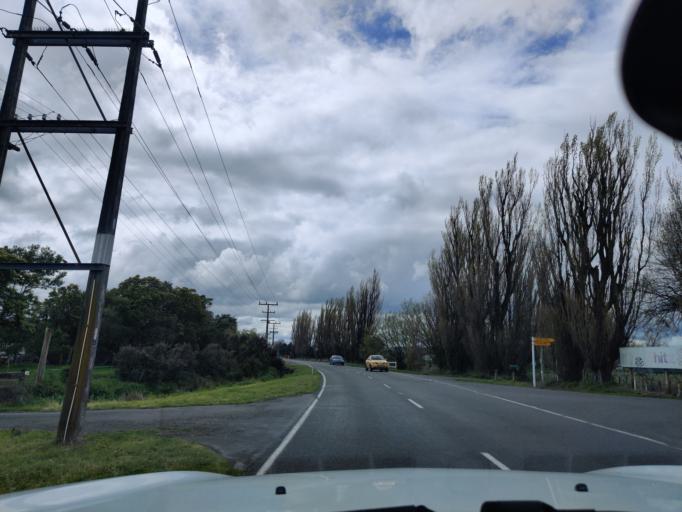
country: NZ
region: Manawatu-Wanganui
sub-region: Palmerston North City
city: Palmerston North
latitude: -40.2406
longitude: 175.5598
